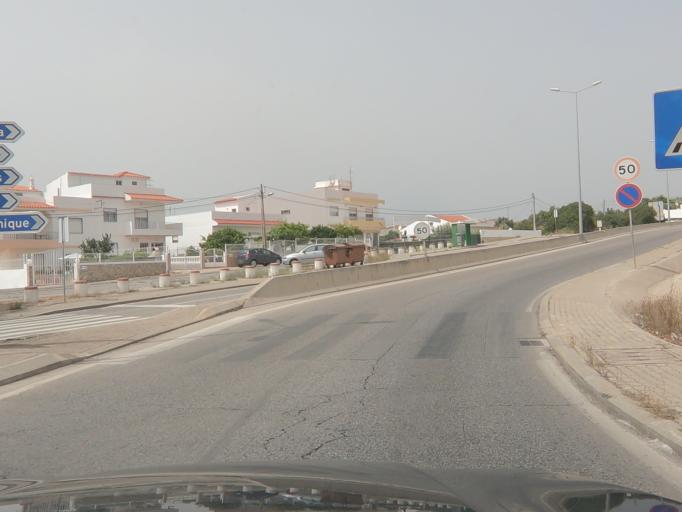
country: PT
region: Faro
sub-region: Portimao
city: Portimao
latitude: 37.1614
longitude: -8.5340
